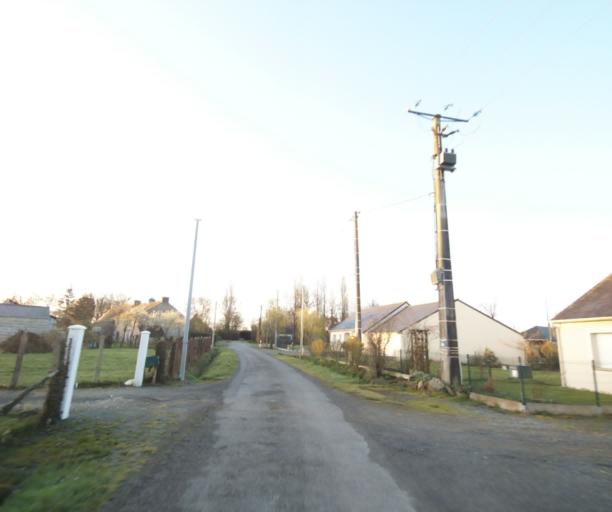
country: FR
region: Pays de la Loire
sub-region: Departement de la Loire-Atlantique
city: Bouvron
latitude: 47.4245
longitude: -1.8828
